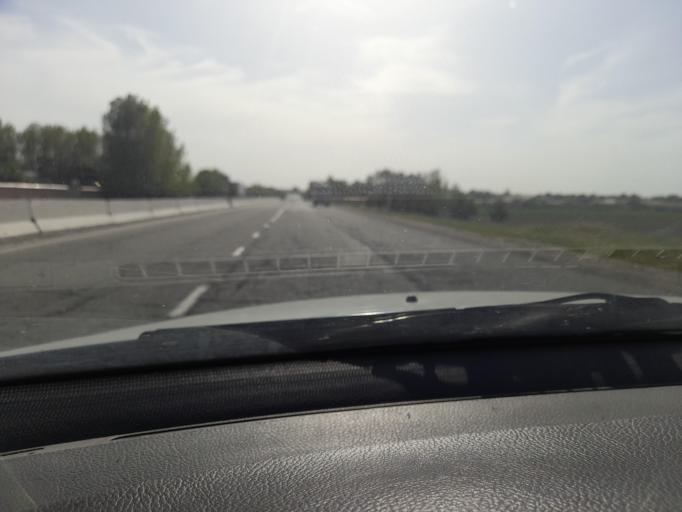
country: UZ
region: Samarqand
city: Kattaqo'rg'on
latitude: 39.9178
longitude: 66.3305
